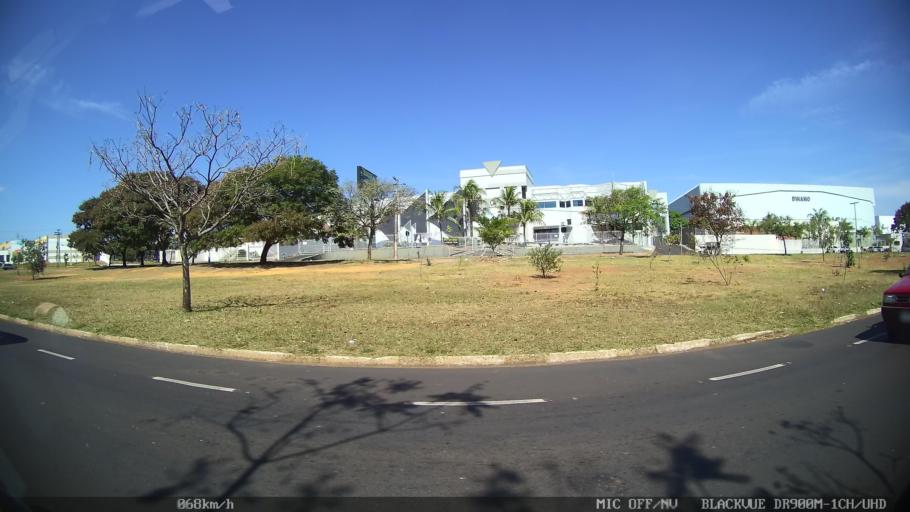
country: BR
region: Sao Paulo
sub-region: Franca
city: Franca
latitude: -20.5482
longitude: -47.4383
